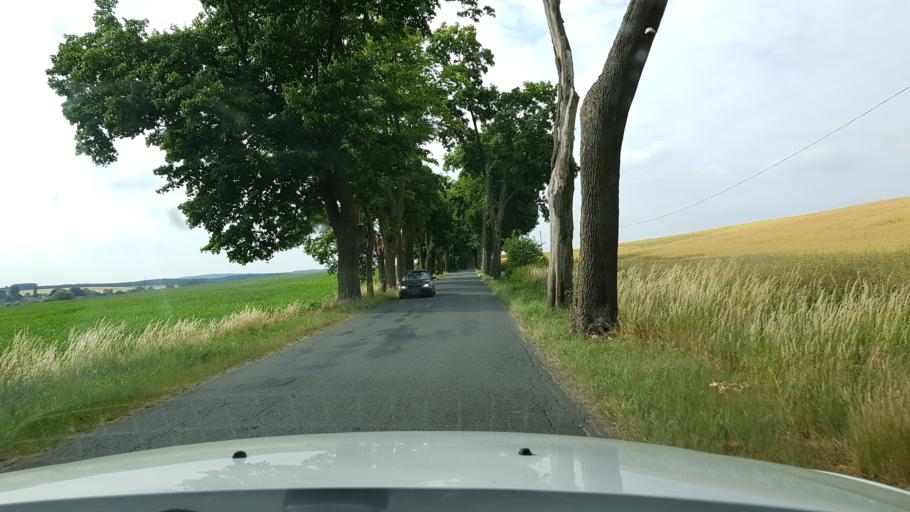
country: PL
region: West Pomeranian Voivodeship
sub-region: Powiat gryfinski
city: Moryn
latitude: 52.9085
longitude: 14.3710
